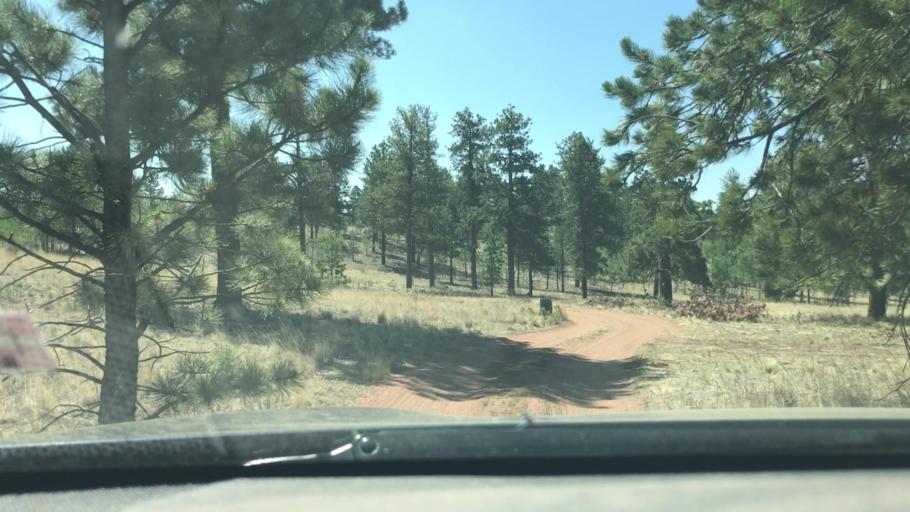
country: US
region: Colorado
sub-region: Teller County
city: Woodland Park
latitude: 38.9991
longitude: -105.3459
